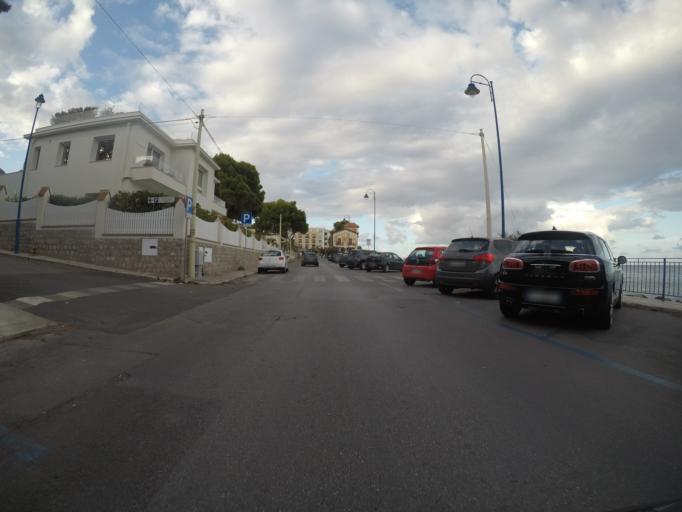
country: IT
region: Sicily
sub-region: Palermo
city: Palermo
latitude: 38.2088
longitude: 13.3288
